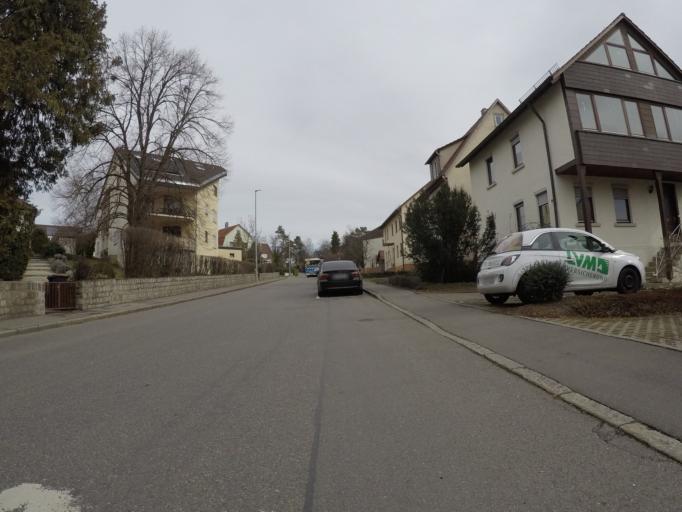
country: DE
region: Baden-Wuerttemberg
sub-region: Tuebingen Region
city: Reutlingen
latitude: 48.5016
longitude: 9.1833
